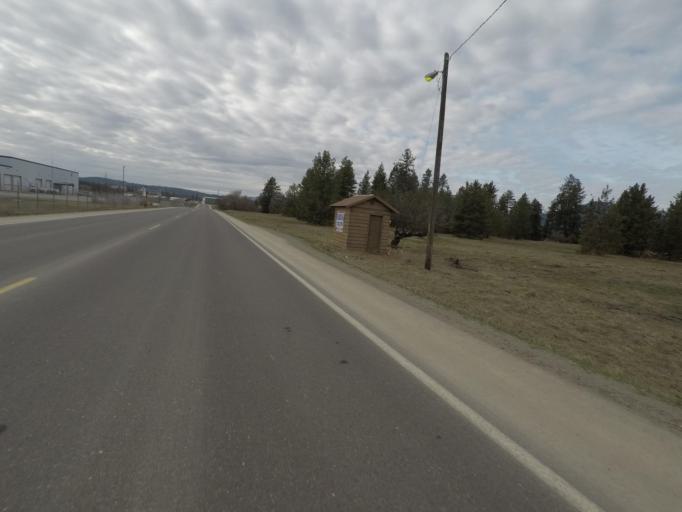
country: US
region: Washington
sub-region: Stevens County
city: Colville
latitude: 48.5506
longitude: -117.8821
